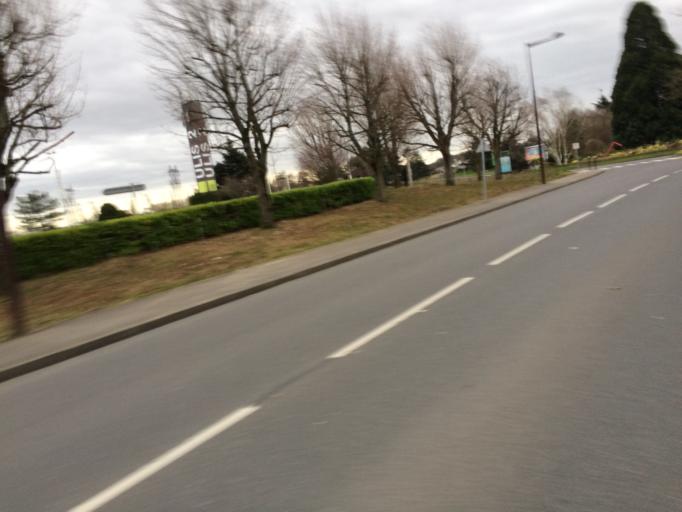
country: FR
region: Ile-de-France
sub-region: Departement de l'Essonne
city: Les Ulis
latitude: 48.6775
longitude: 2.1673
